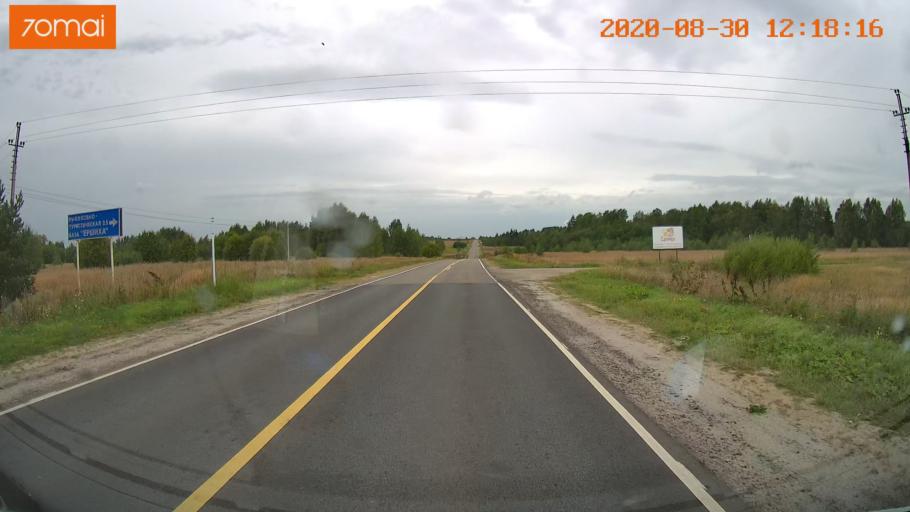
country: RU
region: Ivanovo
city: Yur'yevets
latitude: 57.3234
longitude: 42.9565
